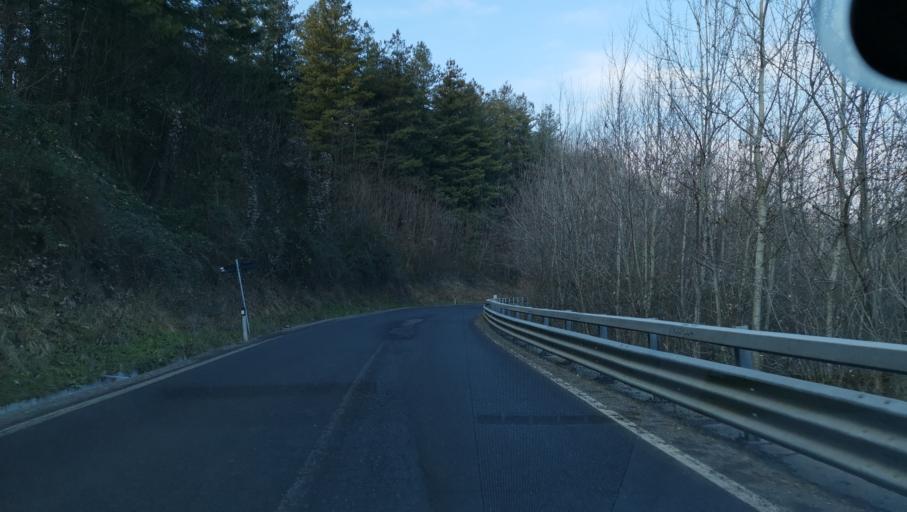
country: IT
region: Piedmont
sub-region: Provincia di Torino
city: Gassino Torinese
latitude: 45.1010
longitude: 7.8438
